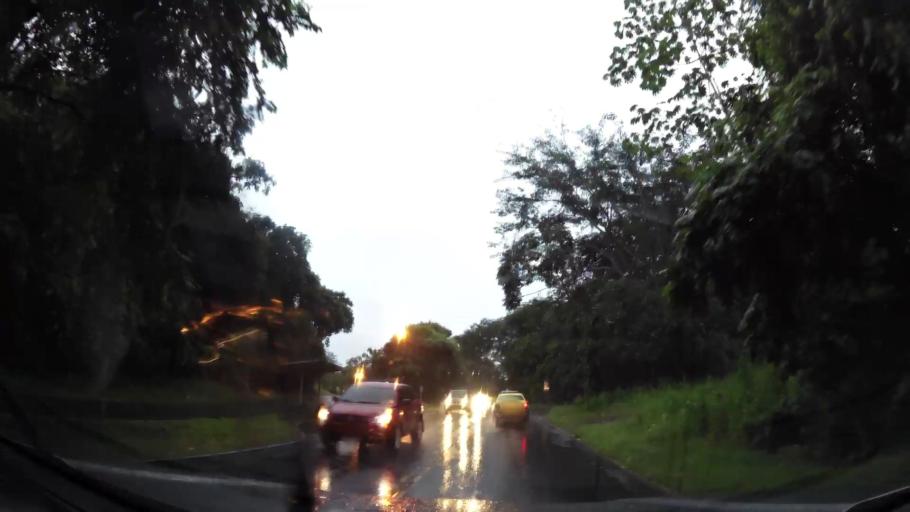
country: PA
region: Panama
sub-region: Distrito de Panama
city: Paraiso
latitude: 9.0065
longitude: -79.5937
